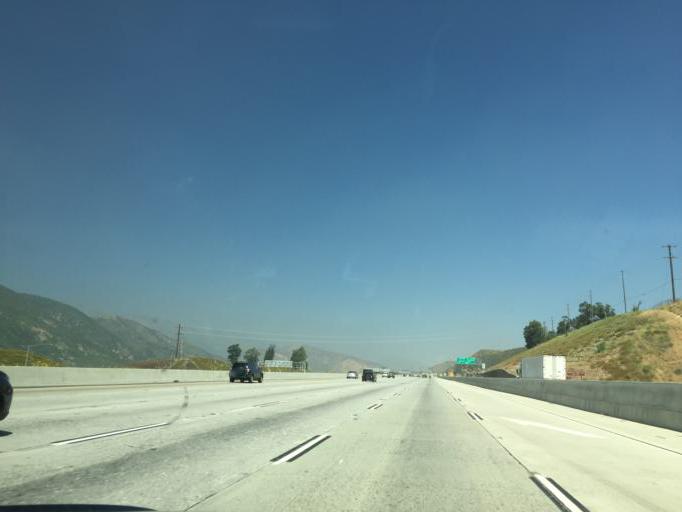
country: US
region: California
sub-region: San Bernardino County
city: Muscoy
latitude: 34.2325
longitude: -117.4192
